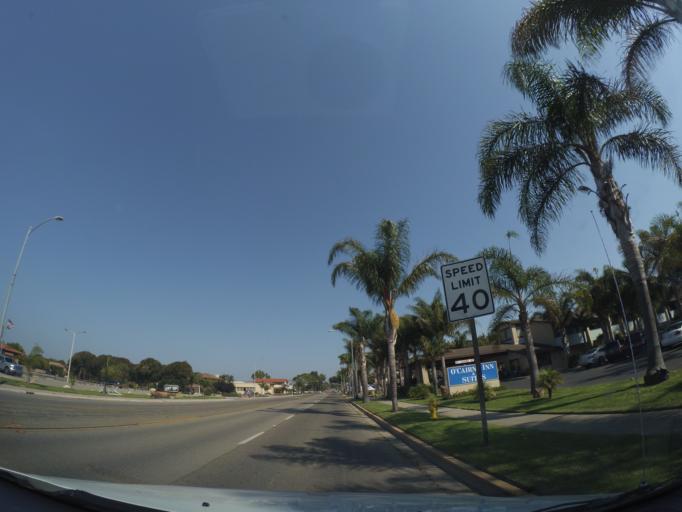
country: US
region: California
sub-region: Santa Barbara County
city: Lompoc
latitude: 34.6388
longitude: -120.4472
